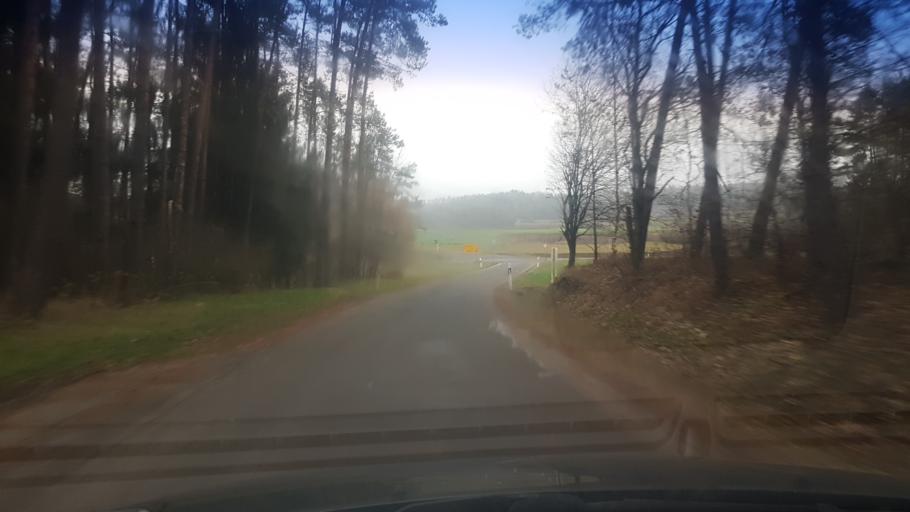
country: DE
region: Bavaria
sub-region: Upper Franconia
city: Weismain
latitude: 50.0522
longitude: 11.2878
